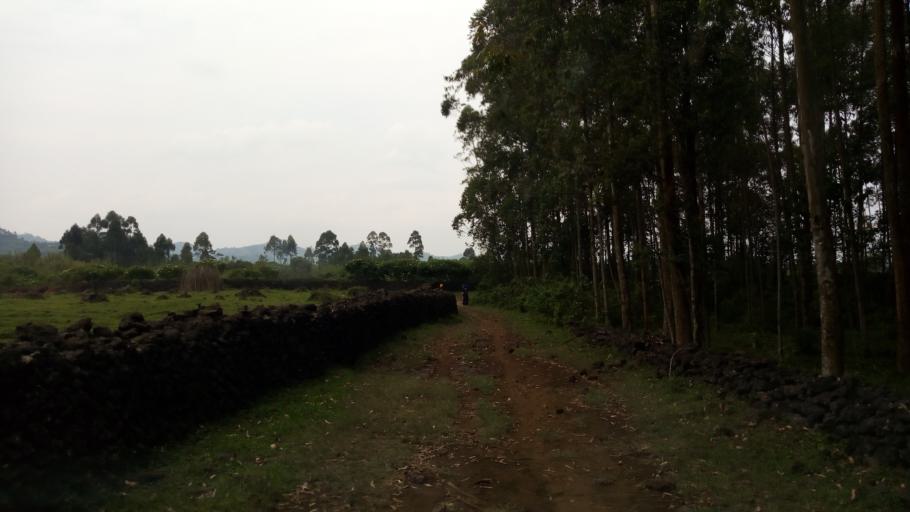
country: UG
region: Western Region
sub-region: Kisoro District
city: Kisoro
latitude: -1.2648
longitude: 29.6052
